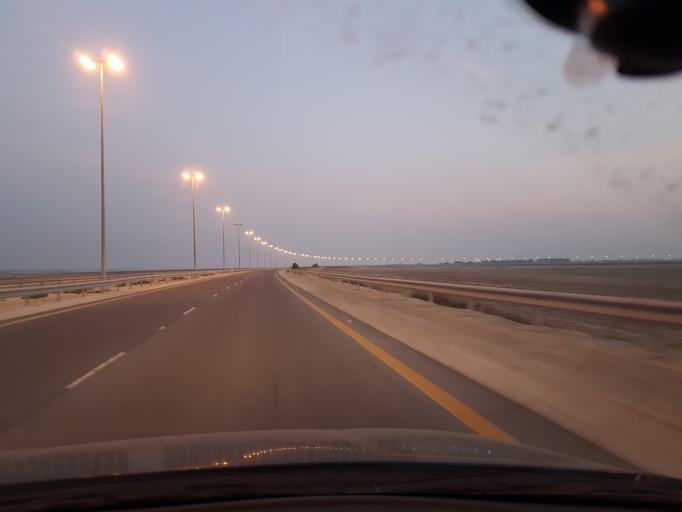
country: BH
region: Central Governorate
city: Dar Kulayb
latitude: 26.0096
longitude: 50.4841
